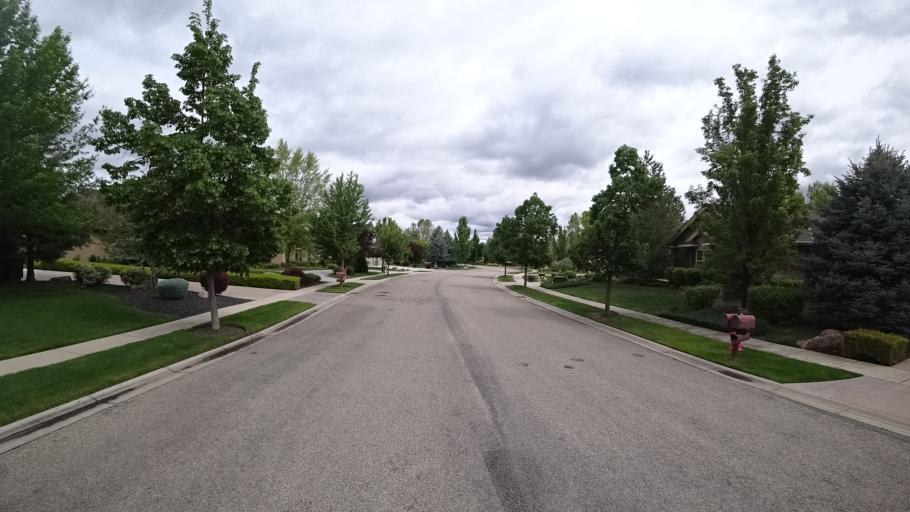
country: US
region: Idaho
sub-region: Ada County
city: Eagle
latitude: 43.6788
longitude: -116.3617
